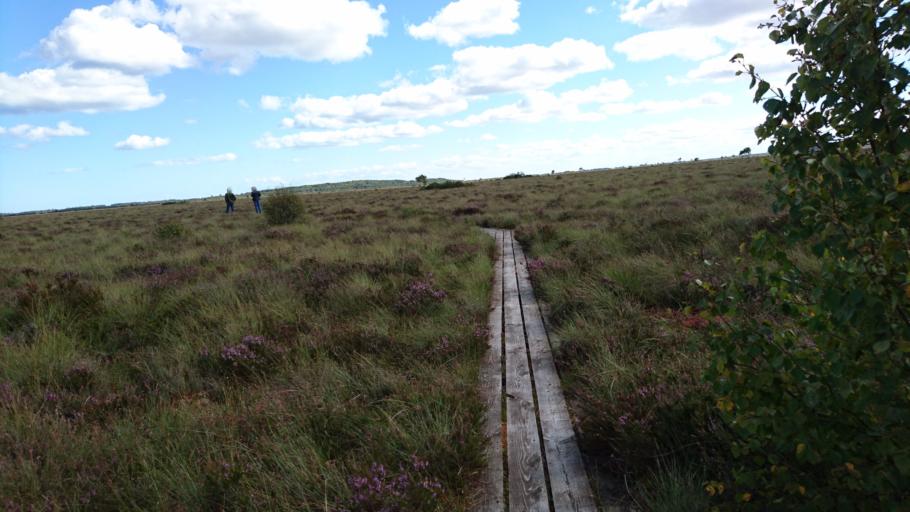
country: DK
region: North Denmark
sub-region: Alborg Kommune
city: Storvorde
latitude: 56.8643
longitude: 10.1700
